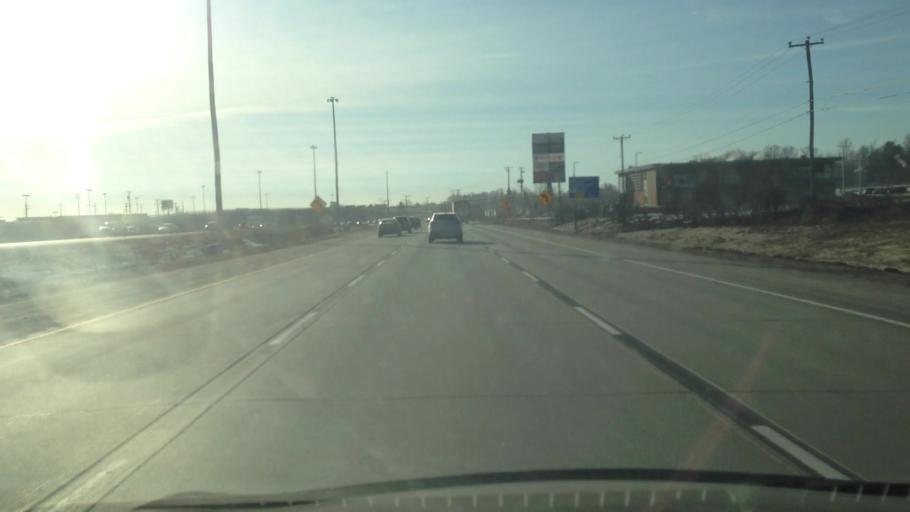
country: CA
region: Quebec
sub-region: Laurentides
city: Saint-Jerome
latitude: 45.7616
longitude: -74.0209
